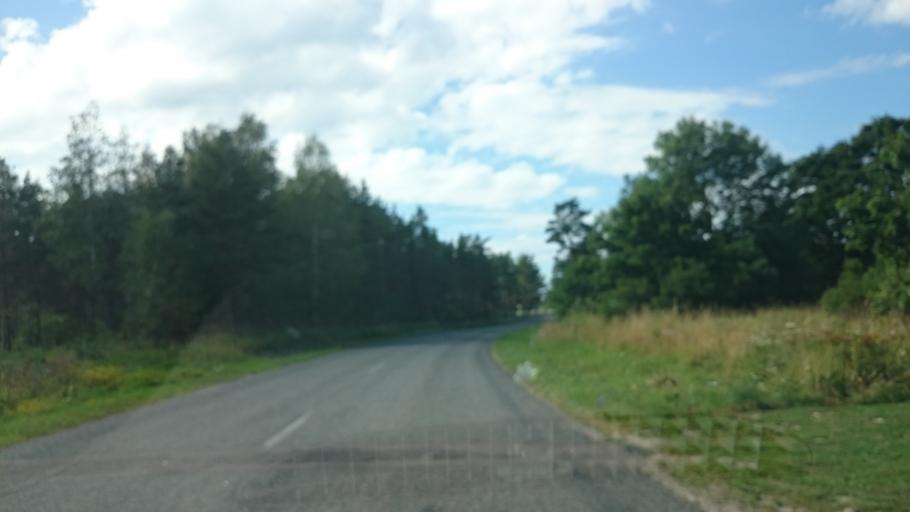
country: EE
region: Saare
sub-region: Orissaare vald
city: Orissaare
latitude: 58.5994
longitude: 22.9802
